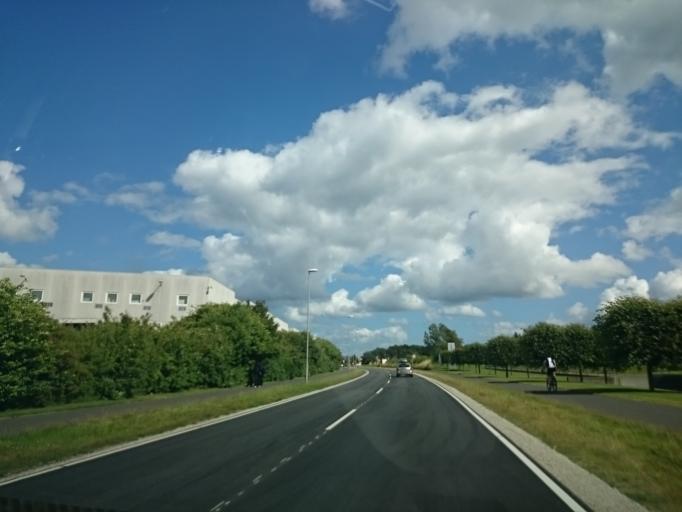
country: DK
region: Central Jutland
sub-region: Arhus Kommune
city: Marslet
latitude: 56.1099
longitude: 10.1627
